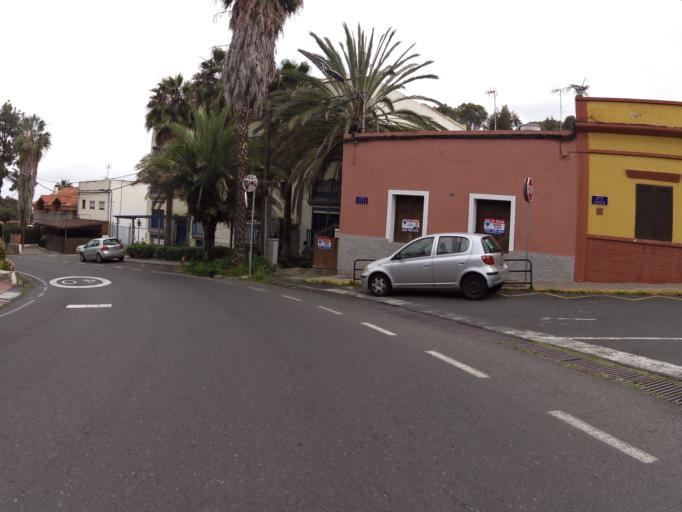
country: ES
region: Canary Islands
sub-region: Provincia de Las Palmas
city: Arucas
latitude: 28.1020
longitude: -15.5290
